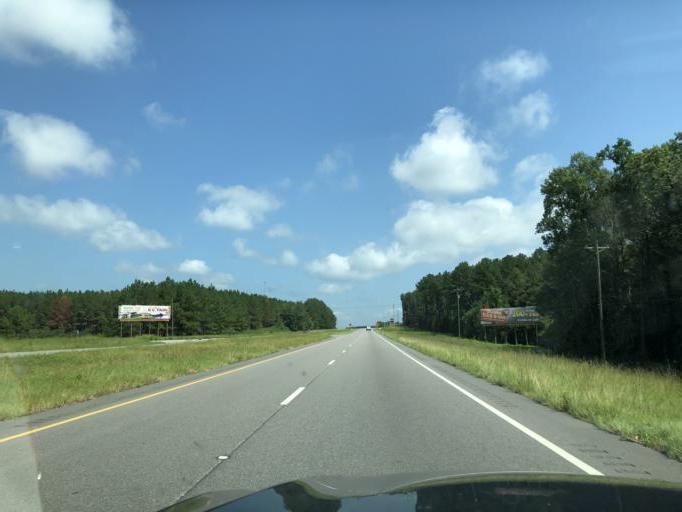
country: US
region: Alabama
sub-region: Houston County
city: Rehobeth
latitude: 31.0567
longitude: -85.4052
